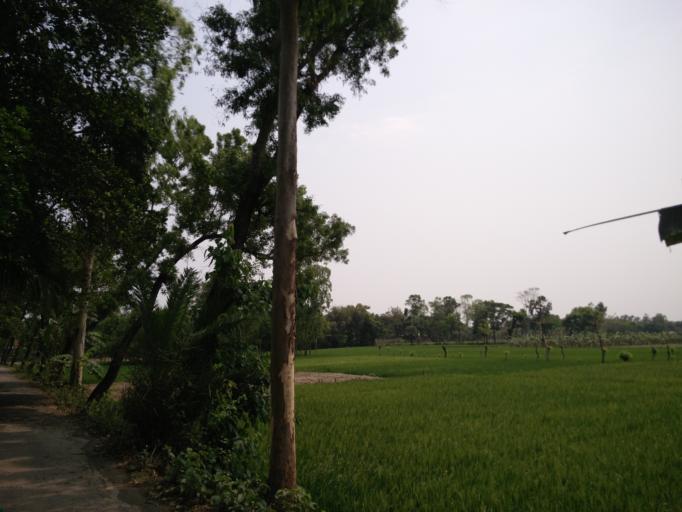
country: BD
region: Dhaka
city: Sherpur
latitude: 24.9336
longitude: 90.1666
